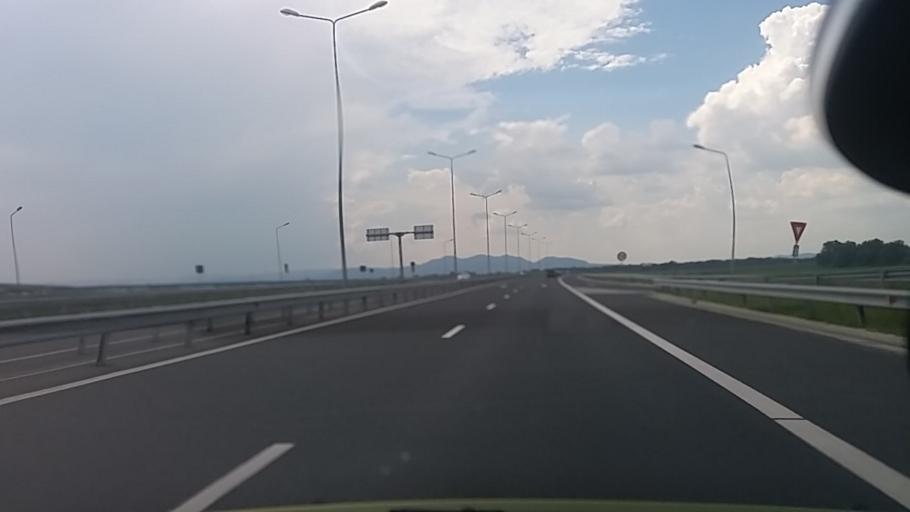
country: RO
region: Hunedoara
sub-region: Oras Simeria
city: Simeria
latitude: 45.8502
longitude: 23.0440
